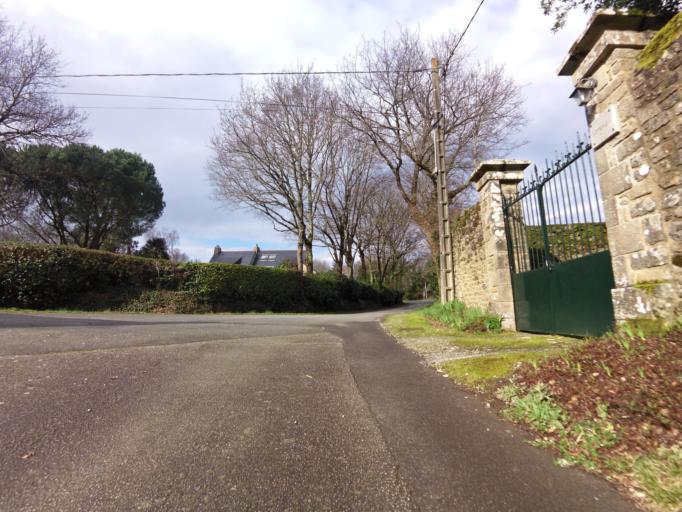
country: FR
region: Brittany
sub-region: Departement du Morbihan
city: Arradon
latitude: 47.6267
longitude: -2.8160
